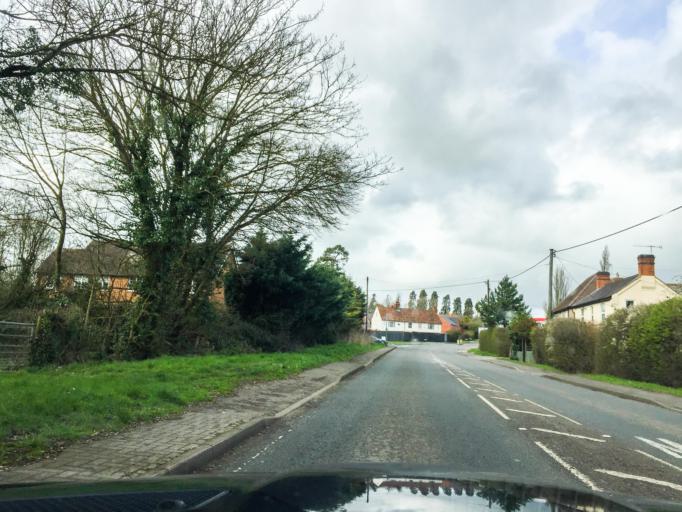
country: GB
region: England
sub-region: Warwickshire
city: Harbury
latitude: 52.1826
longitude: -1.4649
